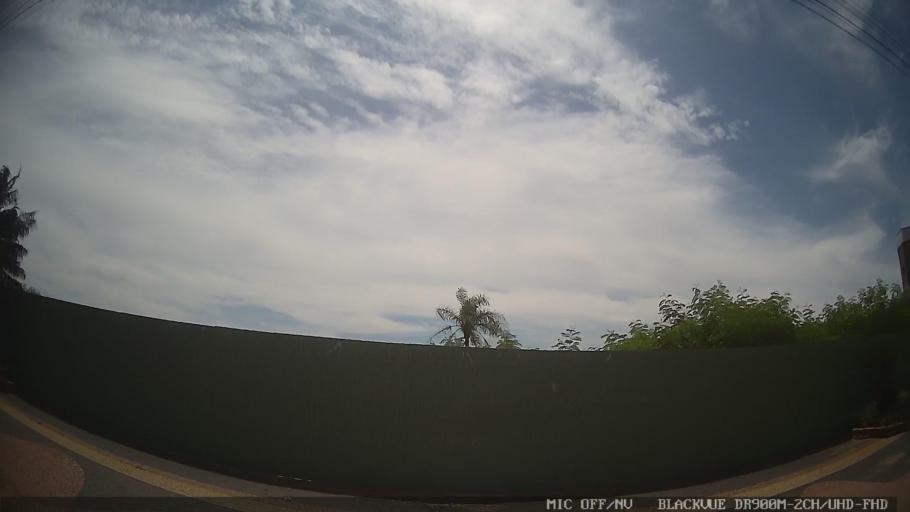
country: BR
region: Sao Paulo
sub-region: Itatiba
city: Itatiba
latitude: -23.0213
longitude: -46.8434
